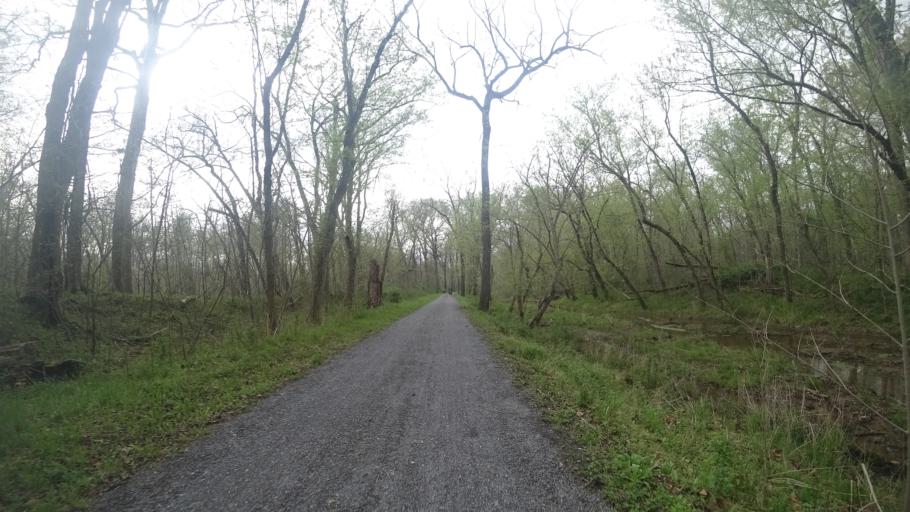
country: US
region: Virginia
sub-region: Loudoun County
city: Belmont
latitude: 39.1184
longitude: -77.4943
